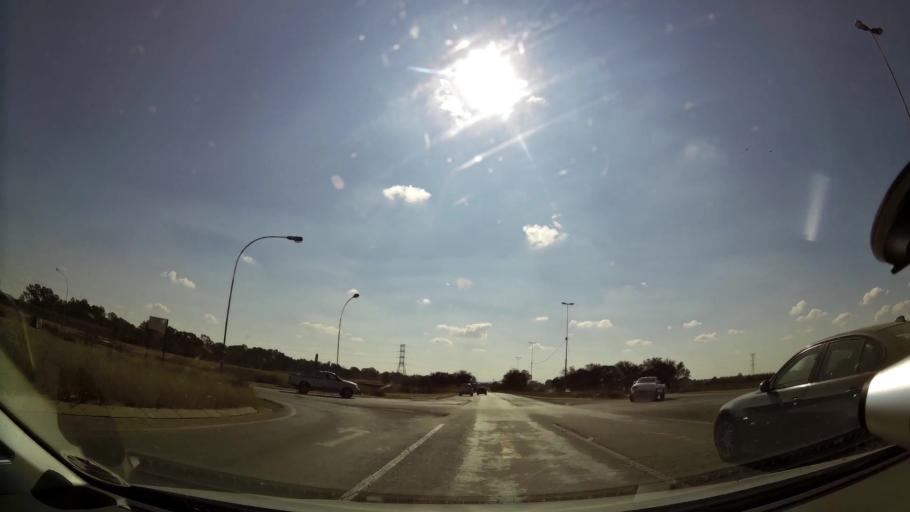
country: ZA
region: Orange Free State
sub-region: Mangaung Metropolitan Municipality
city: Bloemfontein
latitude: -29.1277
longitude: 26.2671
